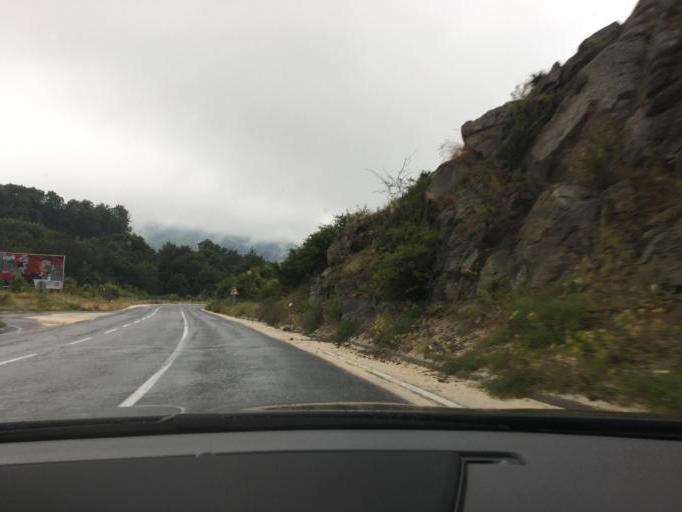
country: MK
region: Kriva Palanka
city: Kriva Palanka
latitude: 42.2187
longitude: 22.4488
